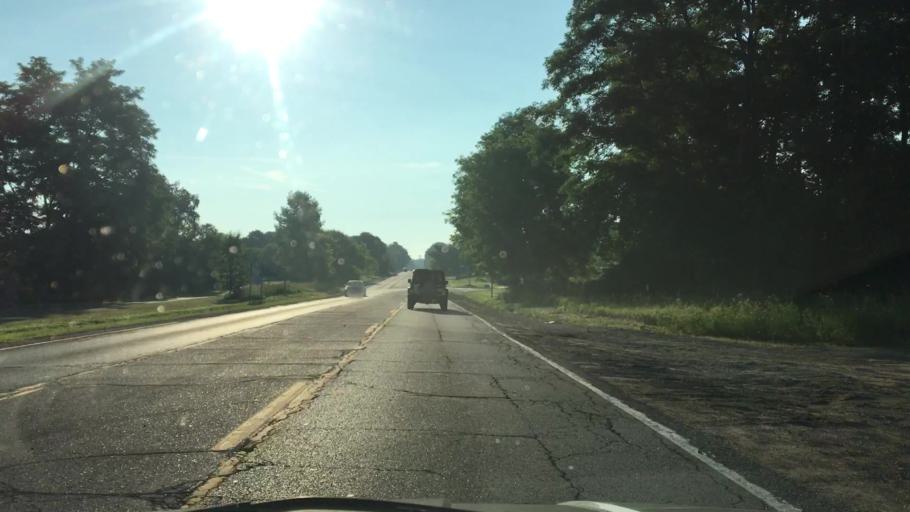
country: US
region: Michigan
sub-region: Oakland County
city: South Lyon
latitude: 42.5166
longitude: -83.6507
